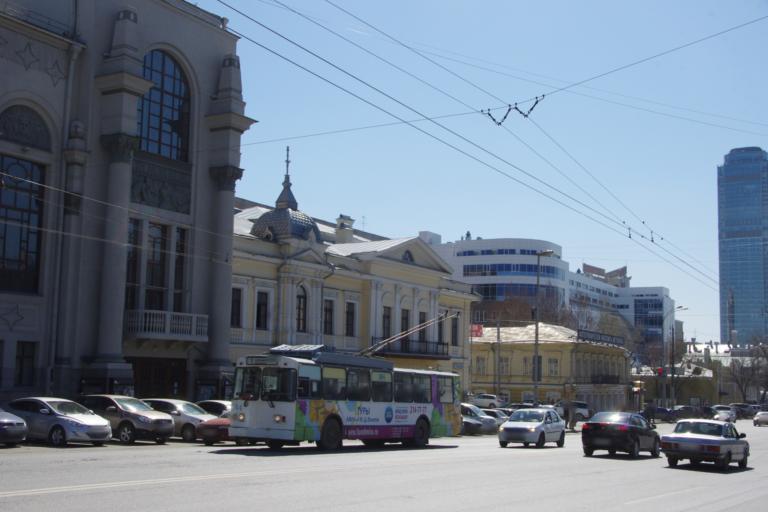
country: RU
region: Sverdlovsk
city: Yekaterinburg
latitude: 56.8428
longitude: 60.6100
